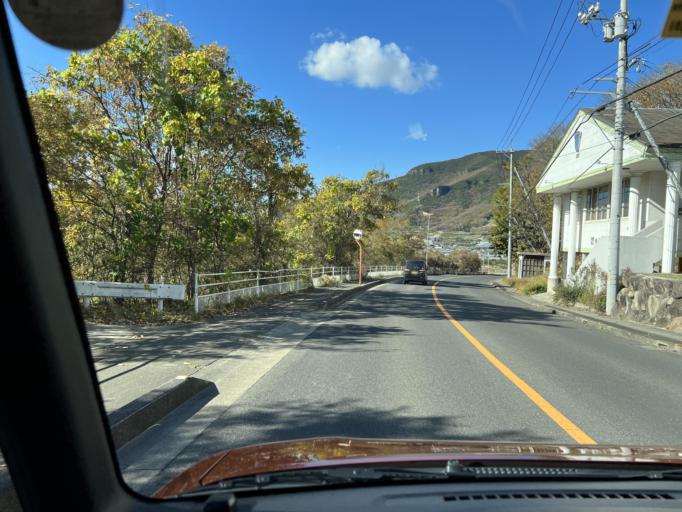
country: JP
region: Kagawa
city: Tonosho
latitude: 34.4812
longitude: 134.2445
